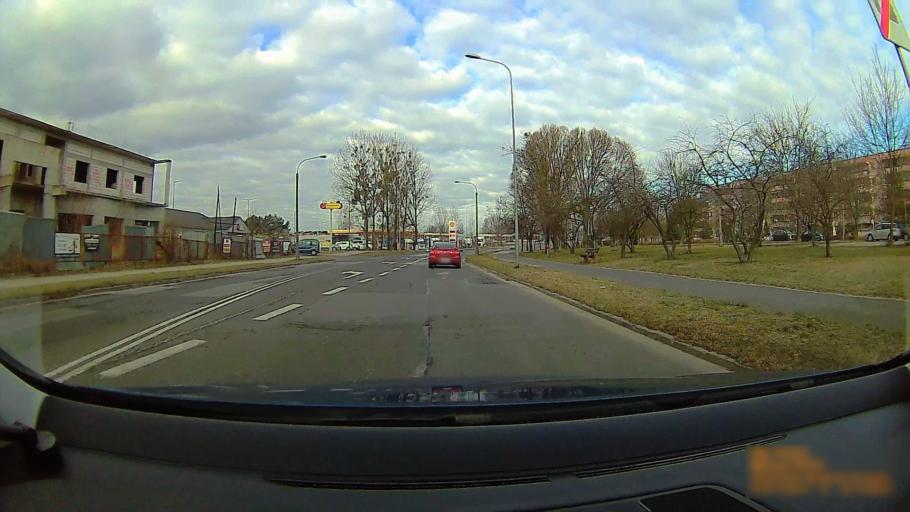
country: PL
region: Greater Poland Voivodeship
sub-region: Konin
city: Konin
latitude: 52.2333
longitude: 18.2496
